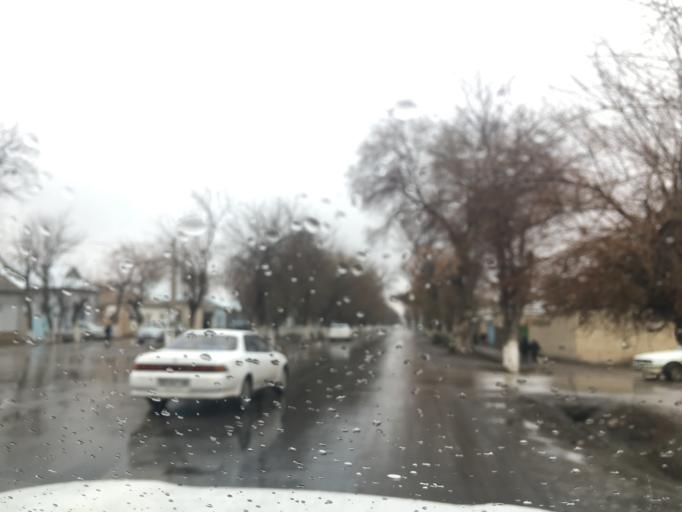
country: TM
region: Mary
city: Yoloeten
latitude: 37.3033
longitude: 62.3566
